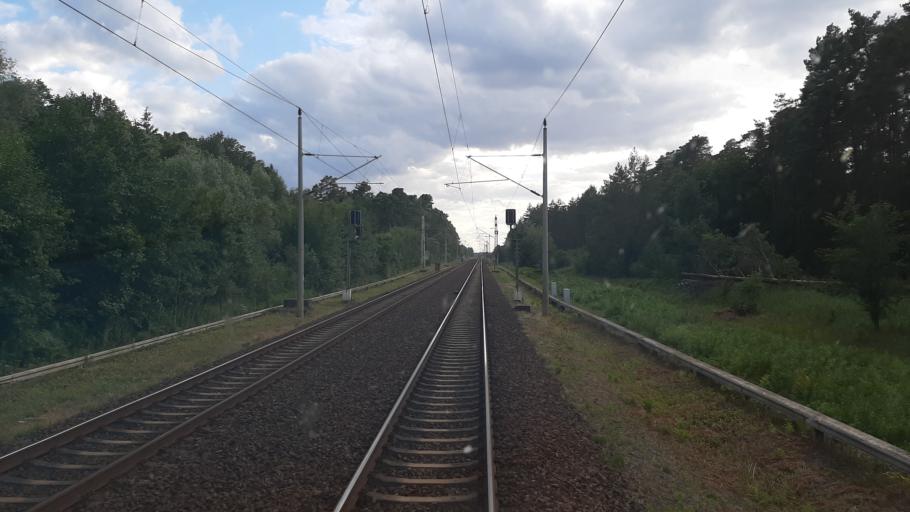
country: DE
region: Brandenburg
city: Falkensee
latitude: 52.6218
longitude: 13.1044
